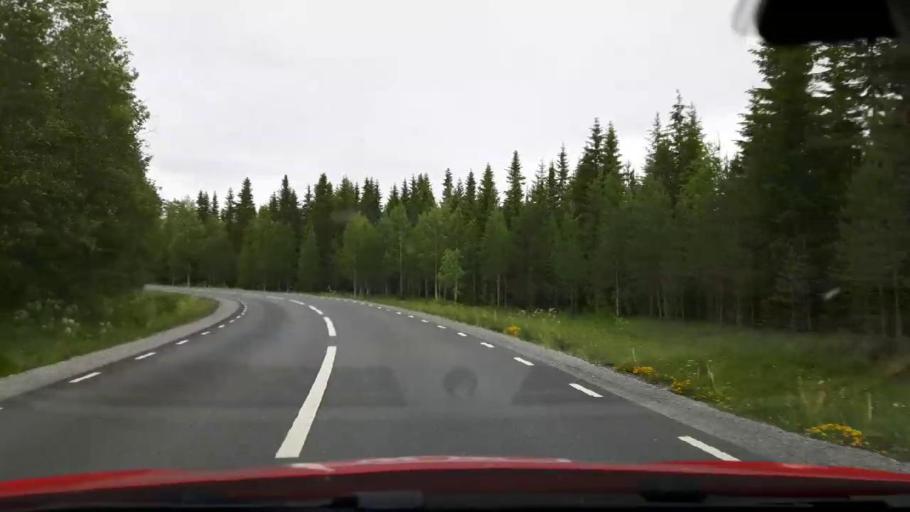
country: SE
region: Jaemtland
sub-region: OEstersunds Kommun
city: Lit
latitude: 63.7421
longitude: 14.8119
